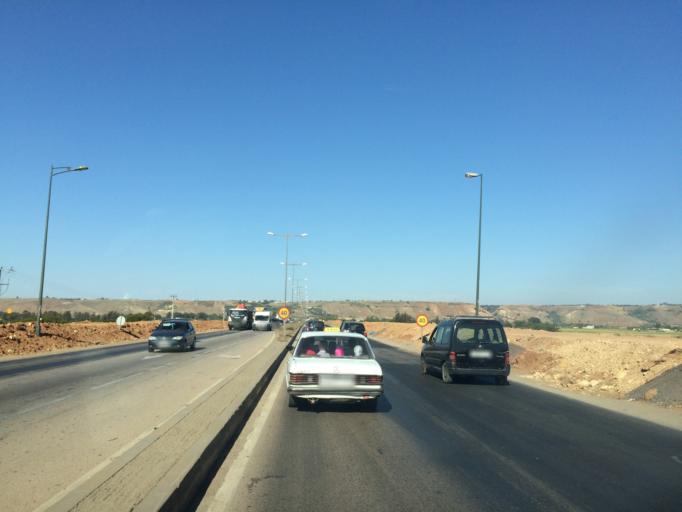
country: MA
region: Rabat-Sale-Zemmour-Zaer
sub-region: Rabat
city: Rabat
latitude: 33.9865
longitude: -6.7899
